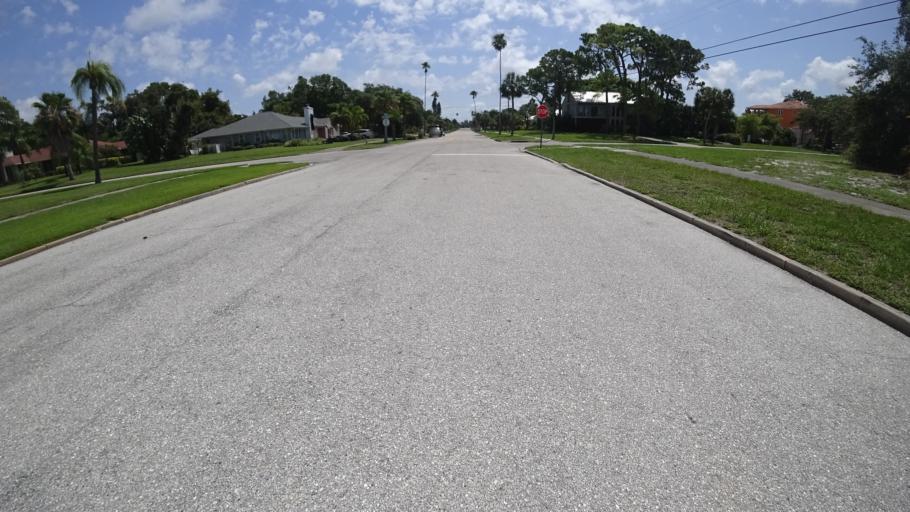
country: US
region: Florida
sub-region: Manatee County
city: Whitfield
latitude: 27.4077
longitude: -82.5746
